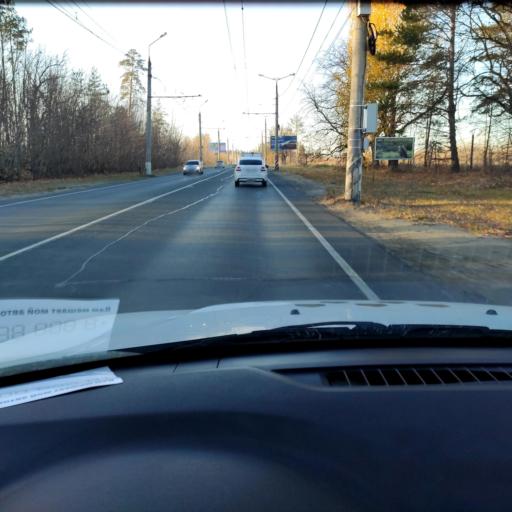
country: RU
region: Samara
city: Tol'yatti
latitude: 53.4891
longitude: 49.3841
